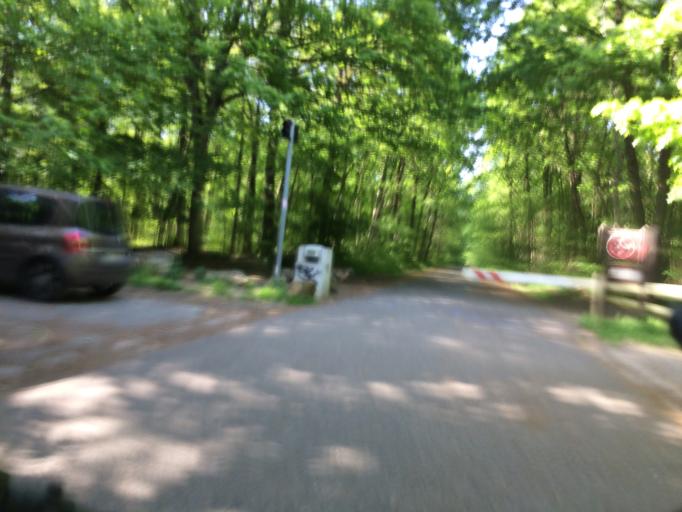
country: FR
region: Ile-de-France
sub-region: Departement de l'Essonne
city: Verrieres-le-Buisson
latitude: 48.7502
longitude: 2.2483
